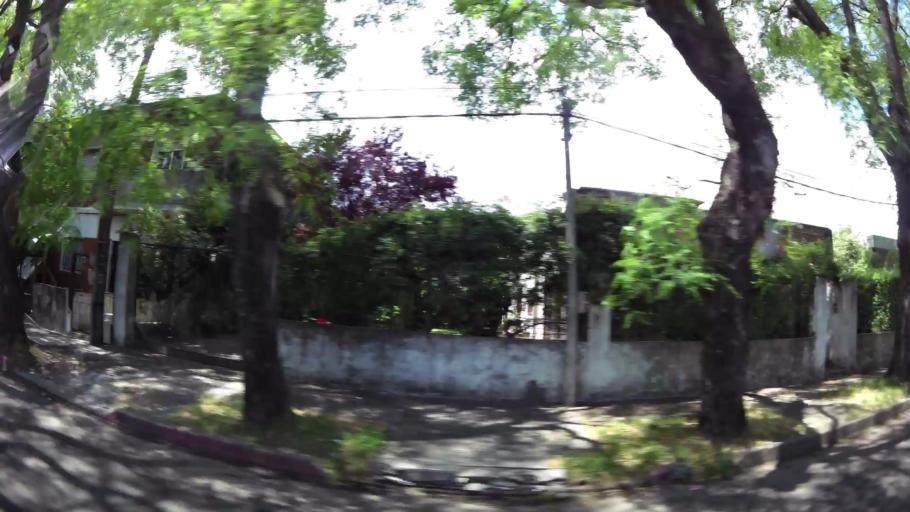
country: UY
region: Montevideo
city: Montevideo
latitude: -34.8646
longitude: -56.1867
